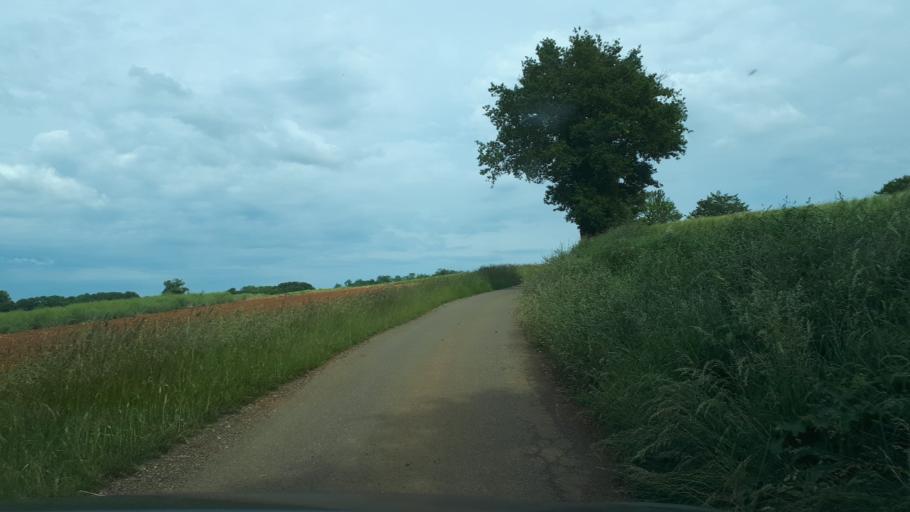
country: FR
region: Centre
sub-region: Departement du Cher
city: Sancerre
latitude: 47.3251
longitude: 2.7215
